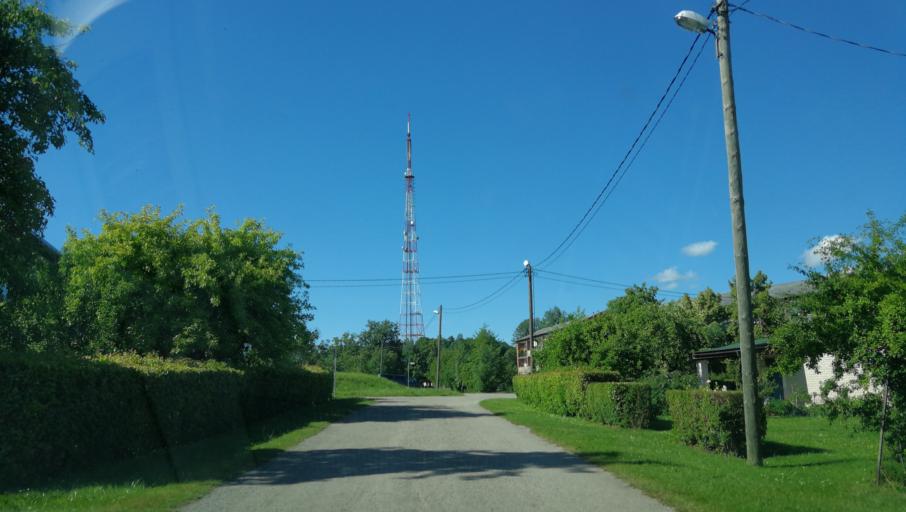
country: LV
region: Cesvaine
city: Cesvaine
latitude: 56.9656
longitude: 26.3023
